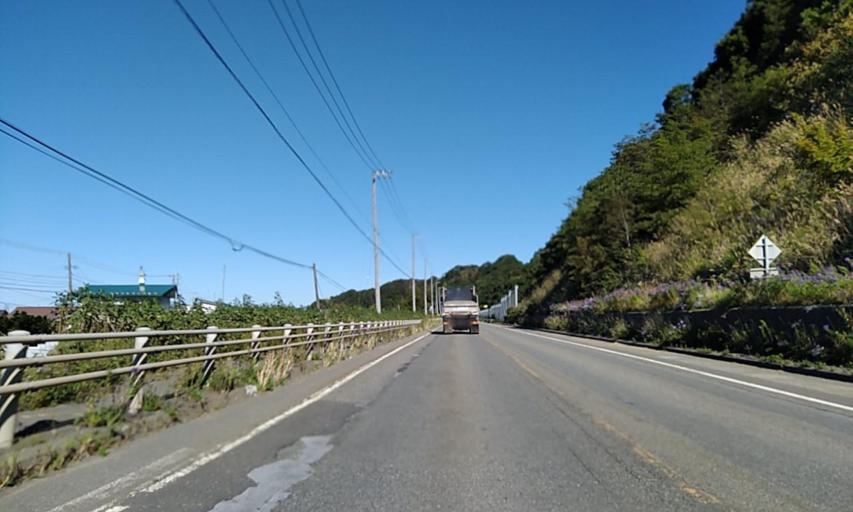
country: JP
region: Hokkaido
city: Shizunai-furukawacho
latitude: 42.4280
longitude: 142.2200
